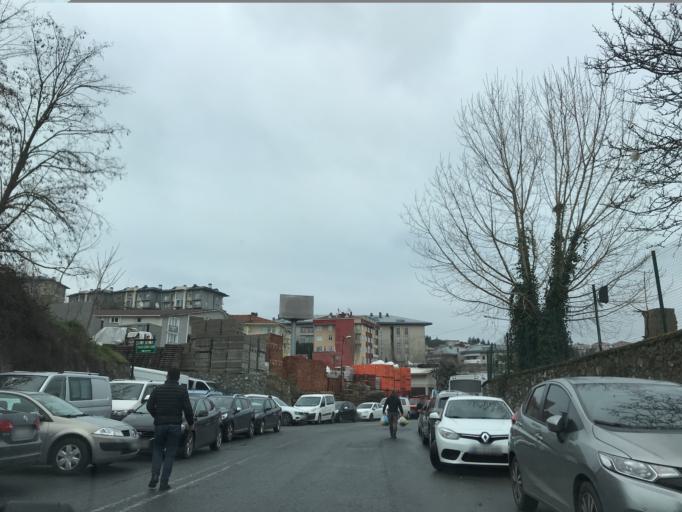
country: TR
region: Istanbul
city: Sisli
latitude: 41.1220
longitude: 29.0467
